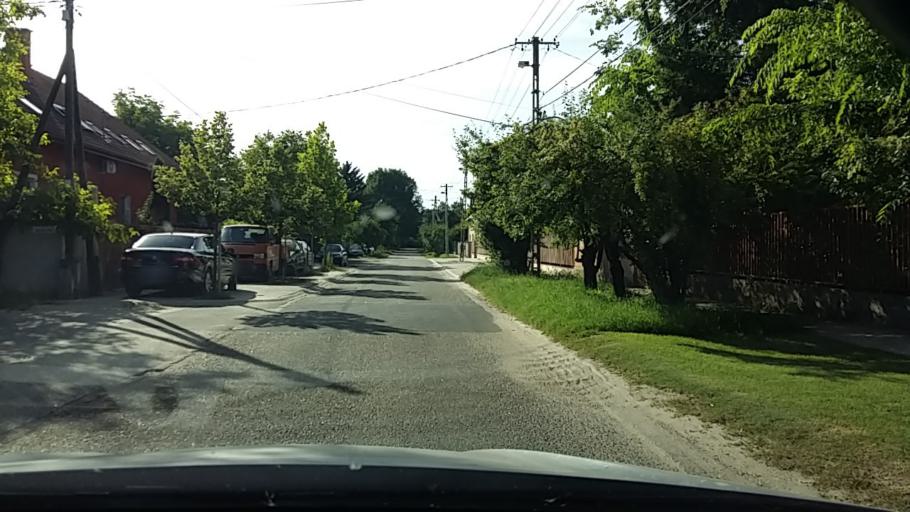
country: HU
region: Pest
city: God
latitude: 47.7000
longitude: 19.1456
